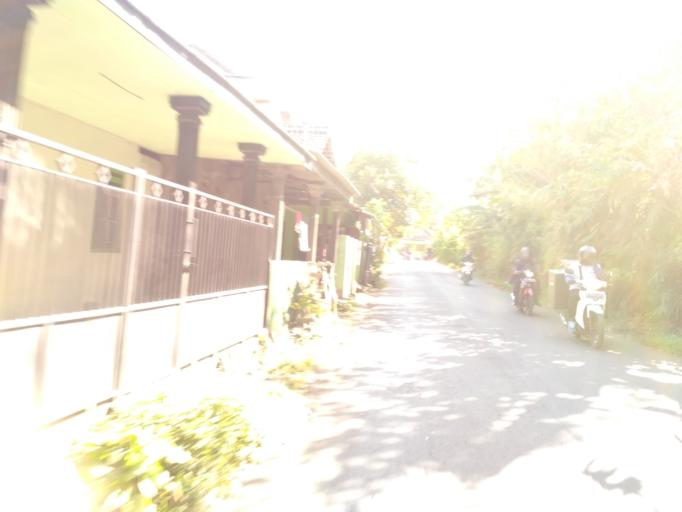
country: ID
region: East Java
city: Singosari
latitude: -7.9279
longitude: 112.6678
